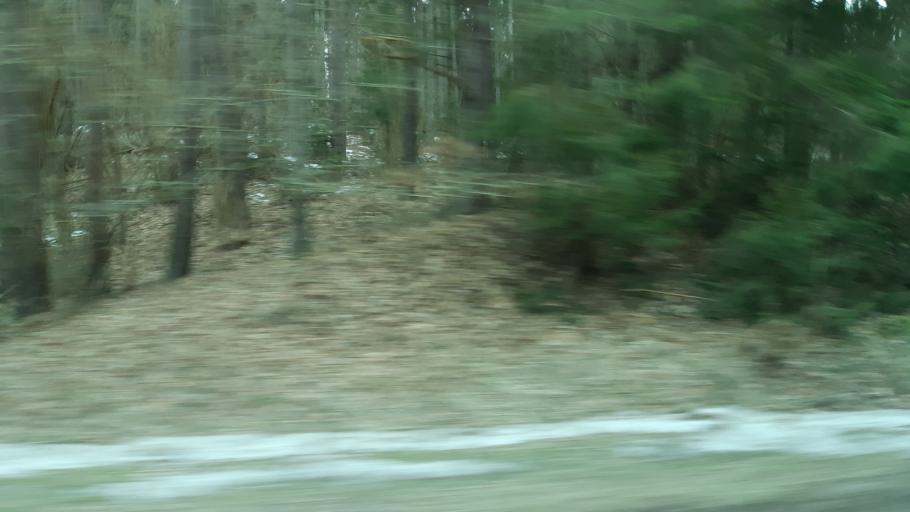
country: PL
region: Podlasie
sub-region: Suwalki
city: Suwalki
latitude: 54.2902
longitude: 22.9552
